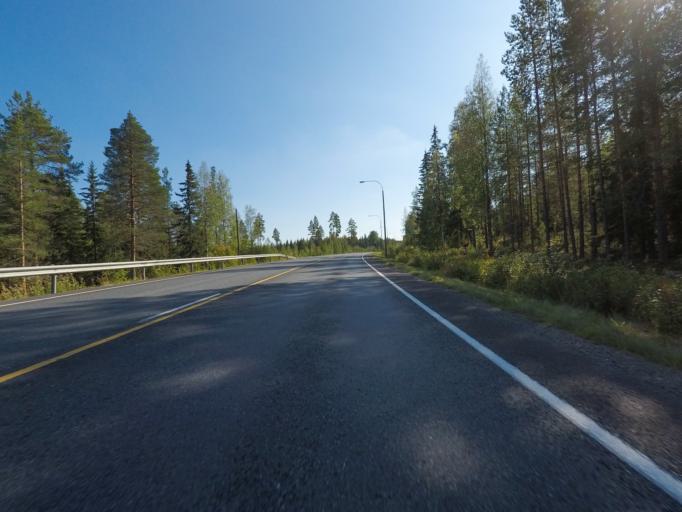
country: FI
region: Northern Savo
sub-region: Varkaus
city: Leppaevirta
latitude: 62.6264
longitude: 27.6209
